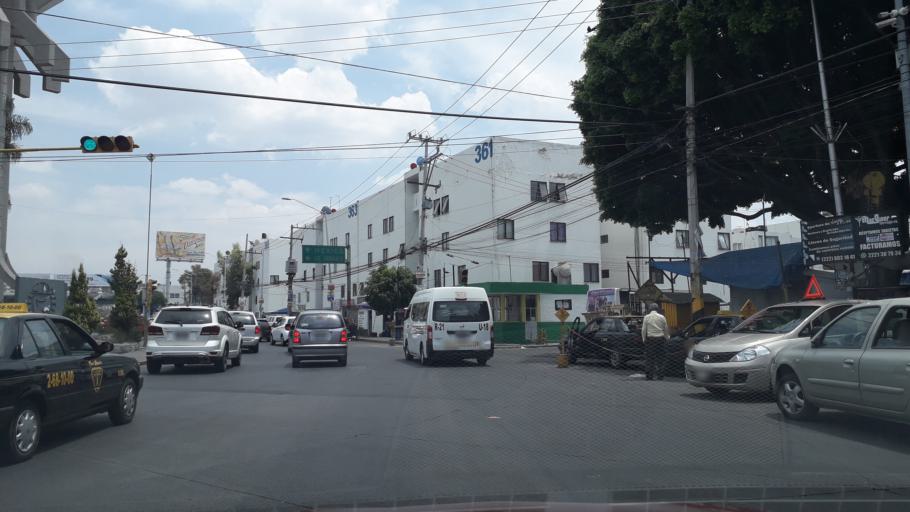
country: MX
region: Puebla
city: Puebla
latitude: 19.0097
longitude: -98.1878
